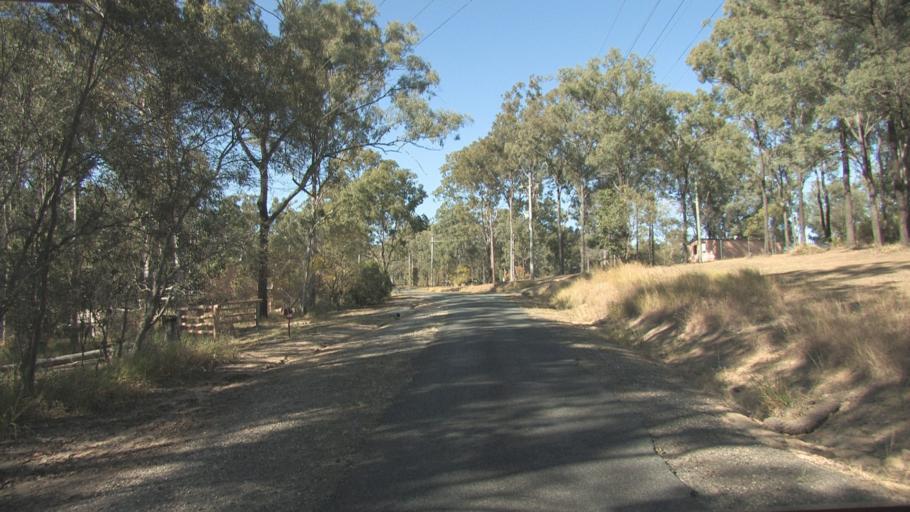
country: AU
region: Queensland
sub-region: Logan
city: Cedar Vale
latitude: -27.8429
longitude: 153.0691
